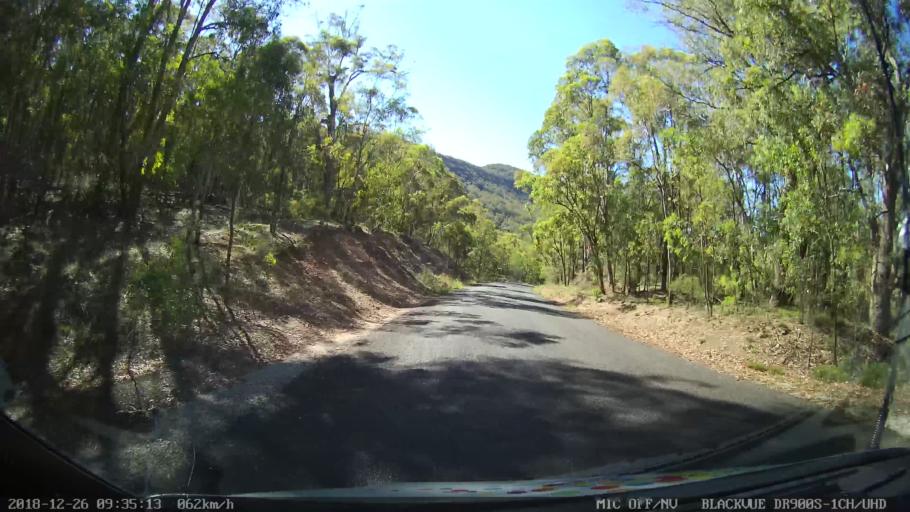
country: AU
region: New South Wales
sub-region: Mid-Western Regional
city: Kandos
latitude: -32.9124
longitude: 150.0398
